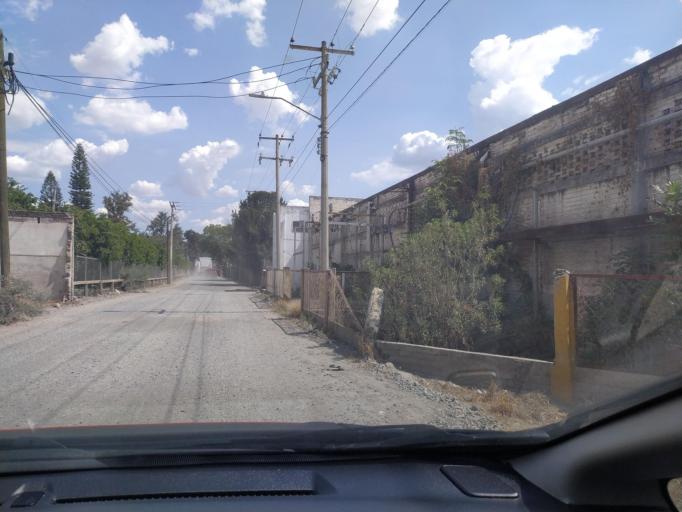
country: MX
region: Guanajuato
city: San Francisco del Rincon
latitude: 21.0264
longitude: -101.8399
